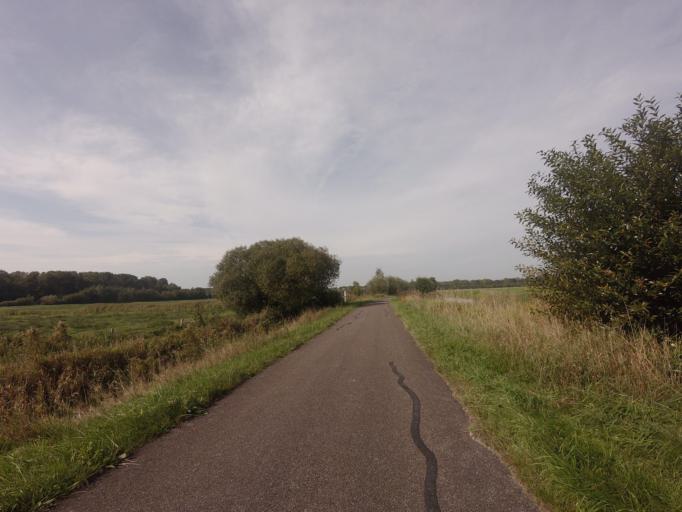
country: NL
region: Groningen
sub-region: Gemeente Leek
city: Leek
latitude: 53.1764
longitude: 6.4023
